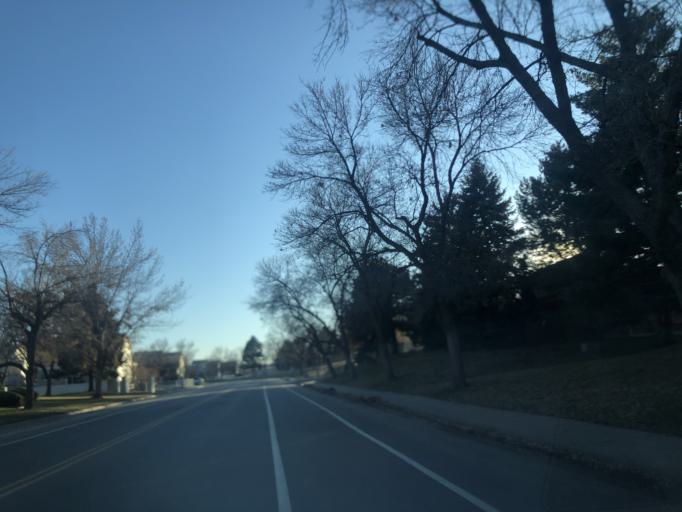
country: US
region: Colorado
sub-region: Adams County
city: Aurora
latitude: 39.7172
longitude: -104.8139
